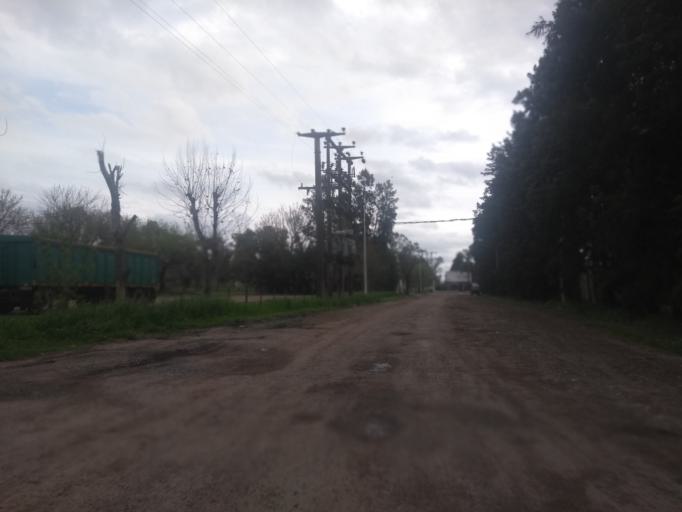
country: AR
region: Santa Fe
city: Galvez
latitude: -31.9078
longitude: -61.2785
